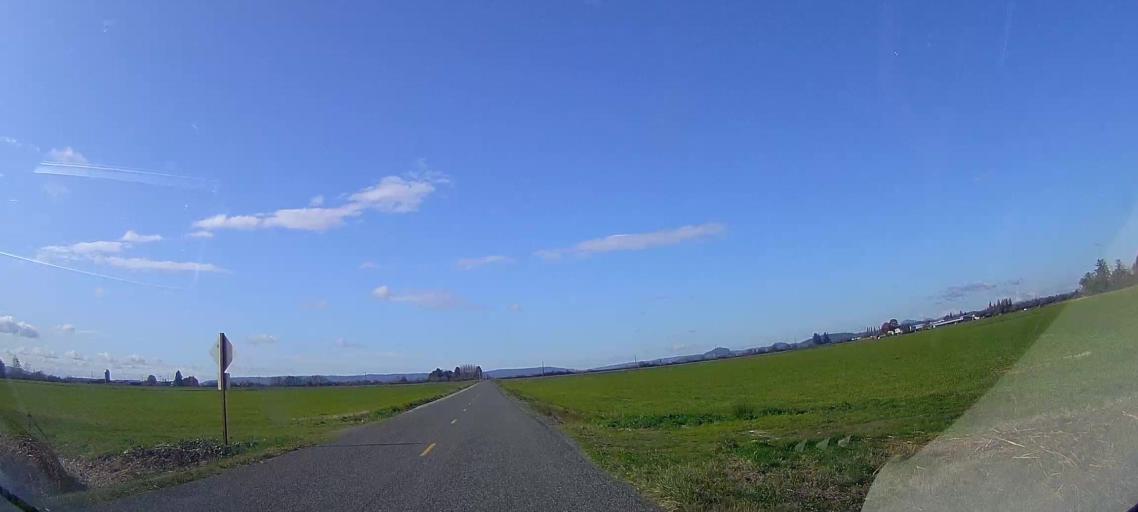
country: US
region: Washington
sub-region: Snohomish County
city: Stanwood
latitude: 48.3299
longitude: -122.3724
